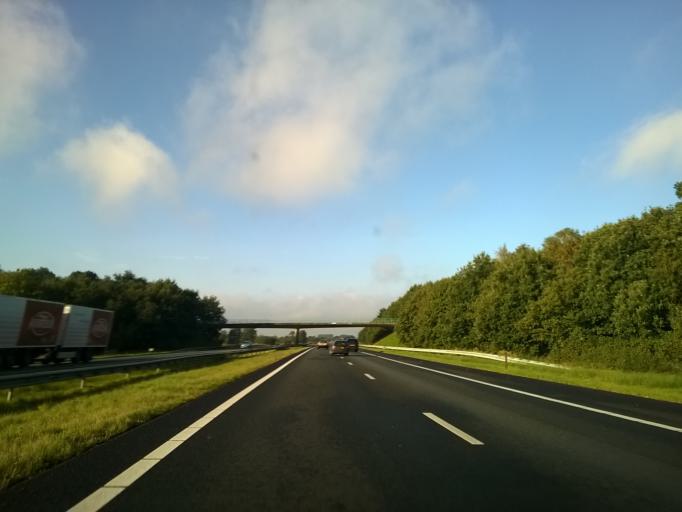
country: NL
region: Groningen
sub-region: Gemeente Leek
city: Leek
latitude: 53.1762
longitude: 6.3547
